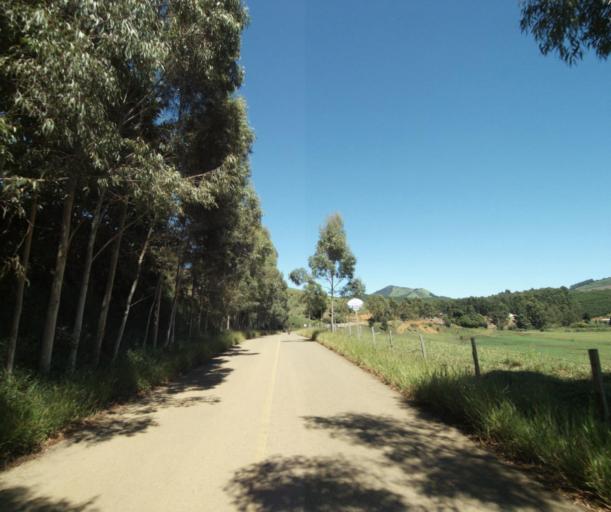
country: BR
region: Minas Gerais
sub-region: Espera Feliz
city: Espera Feliz
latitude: -20.5774
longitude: -41.8330
